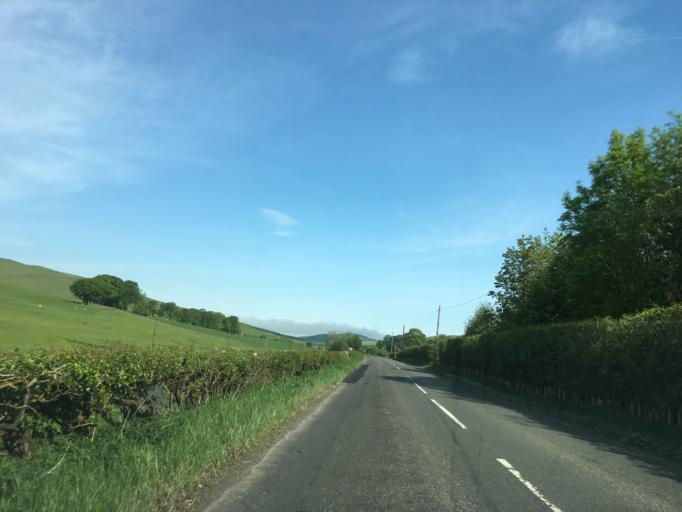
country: GB
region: Scotland
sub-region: South Lanarkshire
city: Biggar
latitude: 55.6203
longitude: -3.4138
